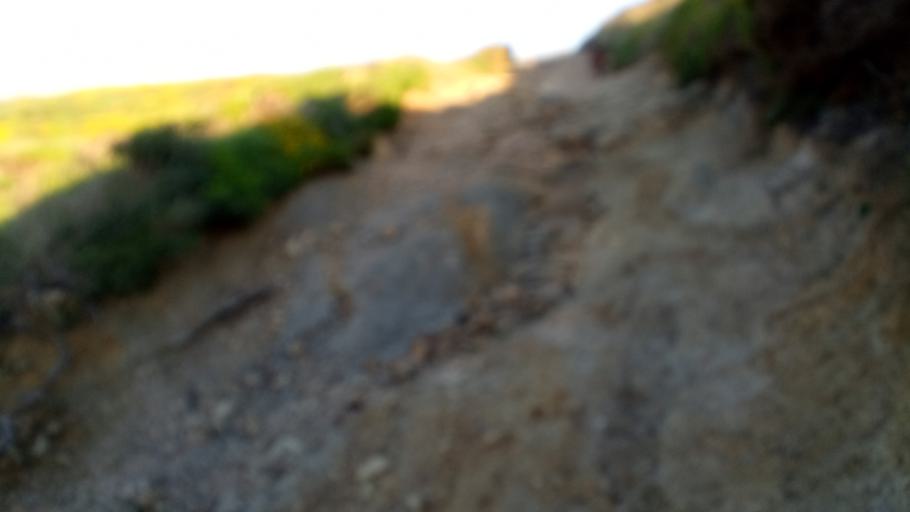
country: PT
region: Leiria
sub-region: Caldas da Rainha
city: Caldas da Rainha
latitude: 39.5019
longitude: -9.1598
